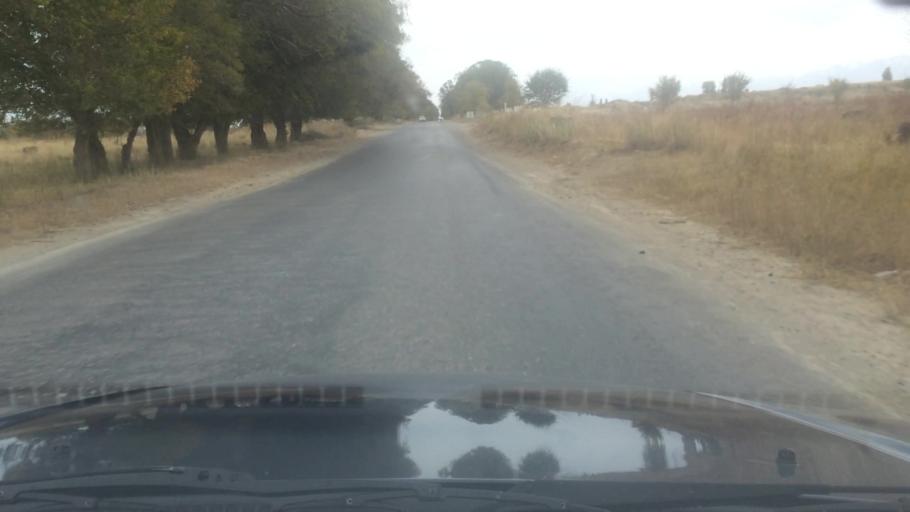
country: KG
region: Ysyk-Koel
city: Balykchy
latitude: 42.3060
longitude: 76.4705
